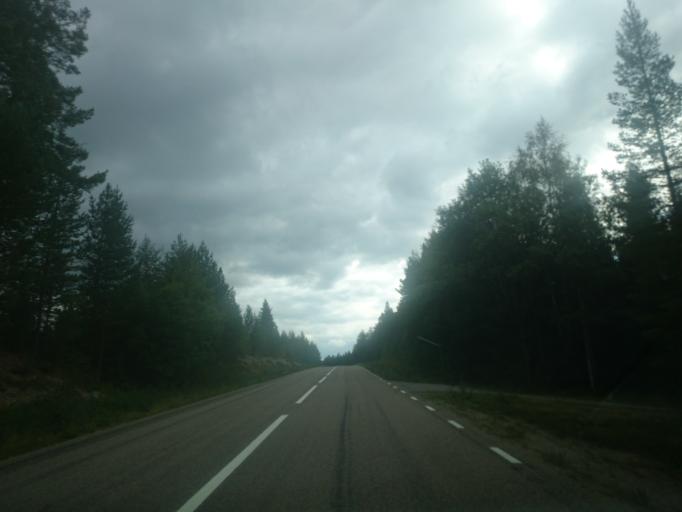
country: SE
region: Jaemtland
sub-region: Harjedalens Kommun
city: Sveg
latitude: 62.2990
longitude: 13.7967
